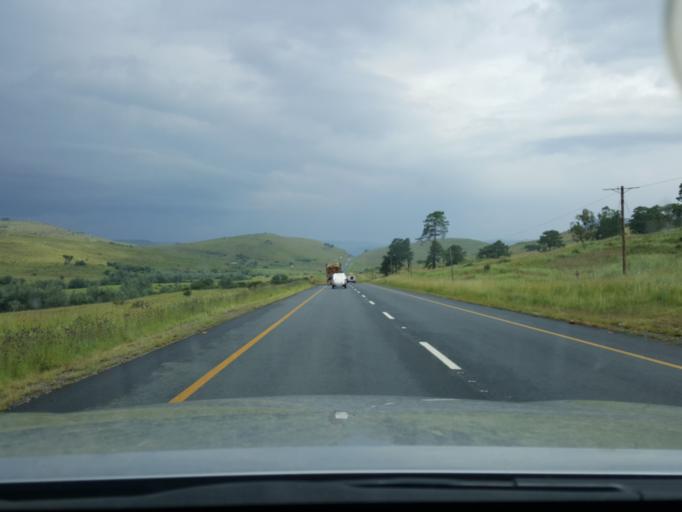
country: ZA
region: Mpumalanga
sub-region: Nkangala District Municipality
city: Belfast
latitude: -25.6186
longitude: 30.2952
